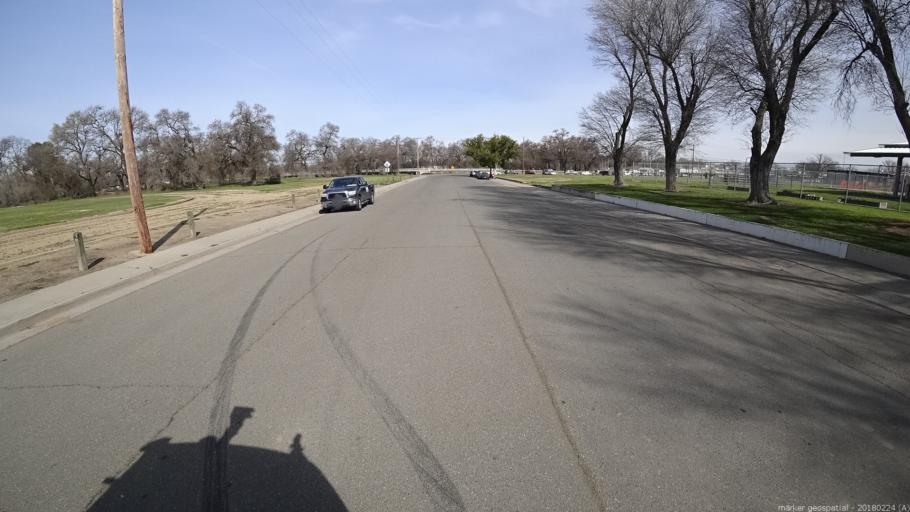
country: US
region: California
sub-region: Sacramento County
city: Rio Linda
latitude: 38.6825
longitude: -121.4431
